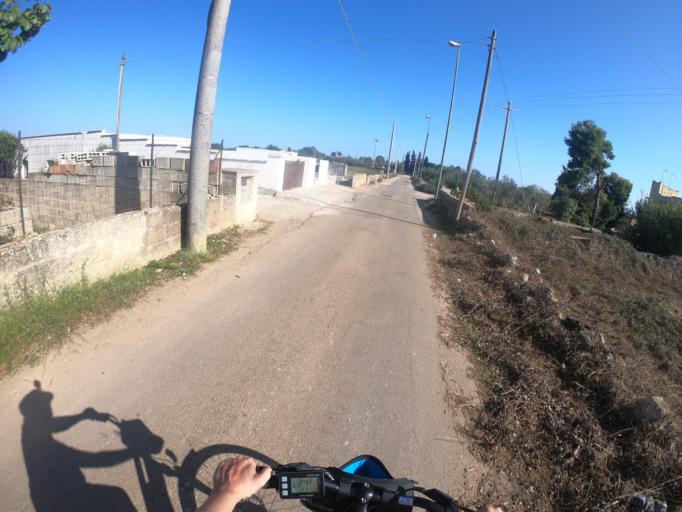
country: IT
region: Apulia
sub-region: Provincia di Lecce
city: Alessano
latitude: 39.8889
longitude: 18.3231
